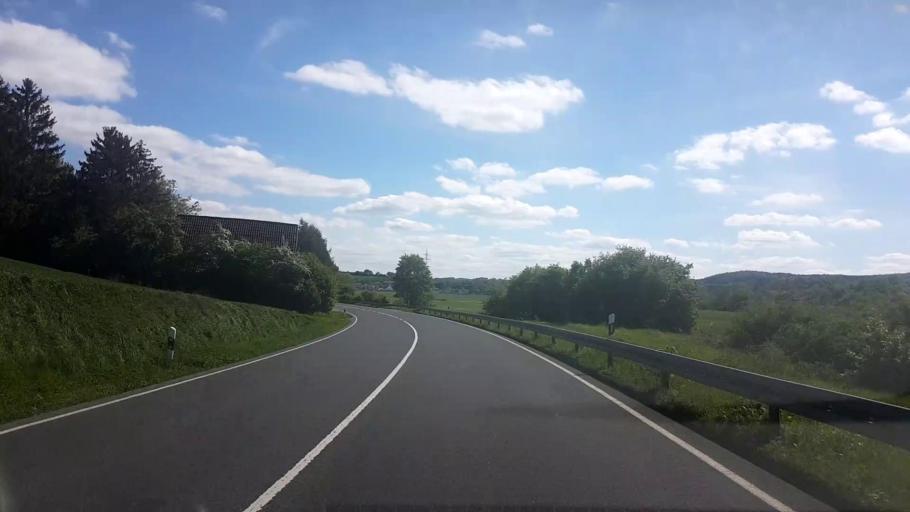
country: DE
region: Bavaria
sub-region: Regierungsbezirk Unterfranken
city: Untermerzbach
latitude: 50.0913
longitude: 10.8628
